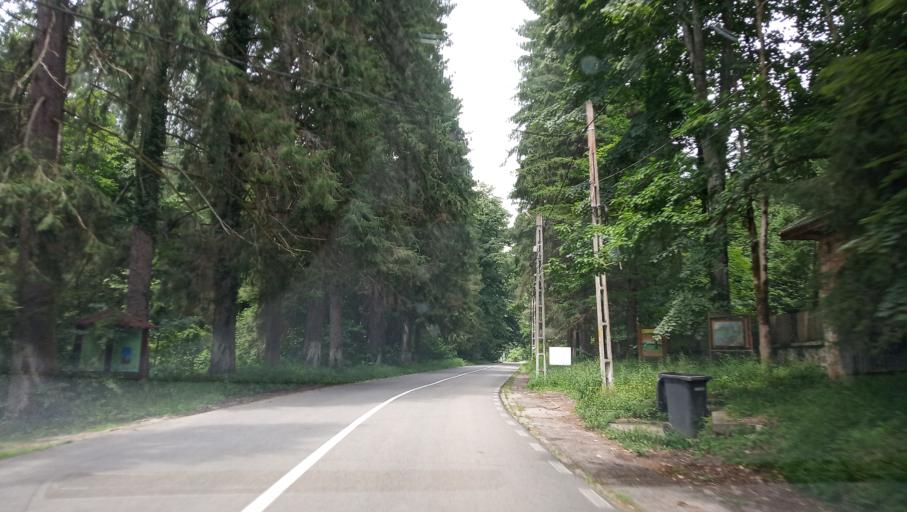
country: RO
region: Gorj
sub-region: Comuna Tismana
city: Pocruia
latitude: 45.0733
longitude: 22.9328
